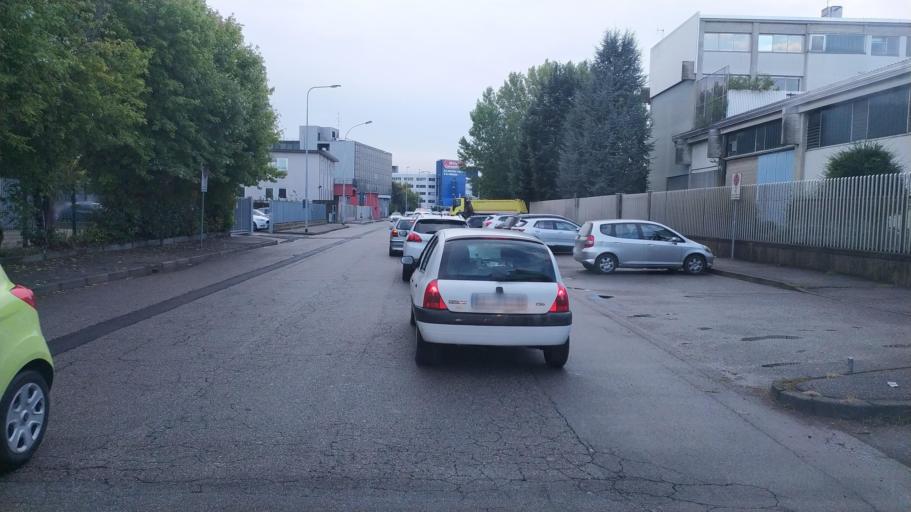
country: IT
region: Lombardy
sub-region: Citta metropolitana di Milano
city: Trezzano sul Naviglio
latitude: 45.4289
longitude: 9.0712
